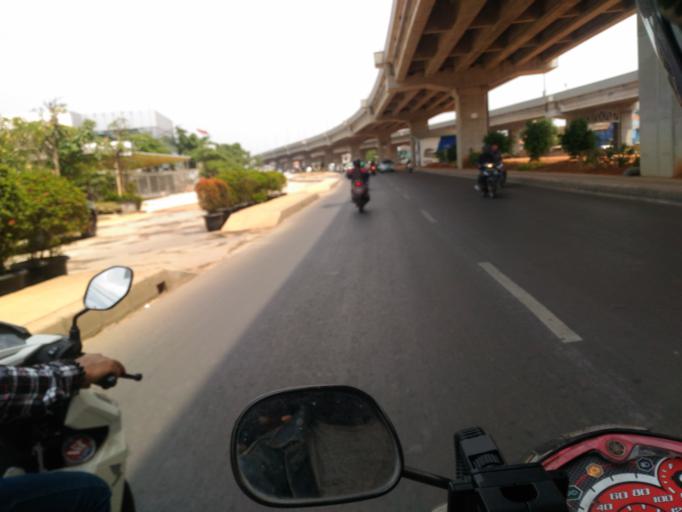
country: ID
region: Jakarta Raya
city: Jakarta
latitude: -6.2433
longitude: 106.8983
